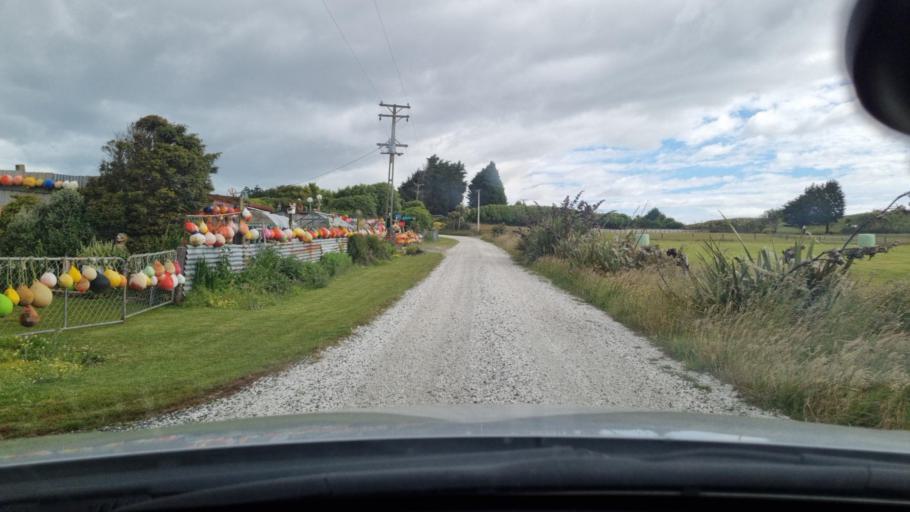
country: NZ
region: Southland
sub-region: Invercargill City
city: Bluff
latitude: -46.5398
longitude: 168.2905
